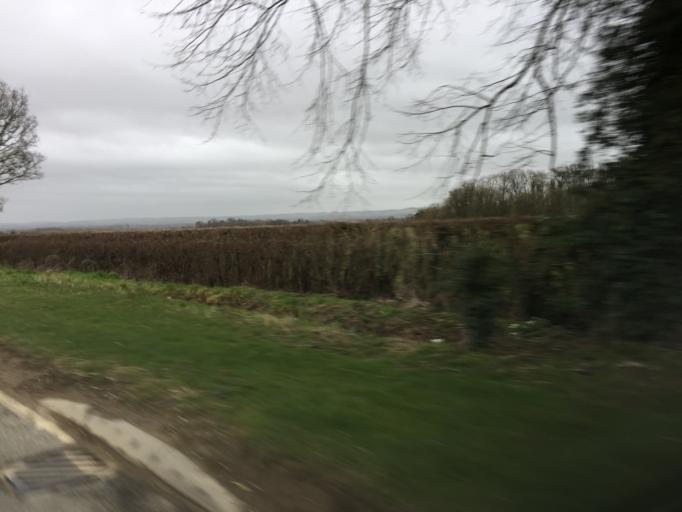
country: GB
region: England
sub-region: Oxfordshire
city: Faringdon
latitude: 51.6493
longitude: -1.5490
